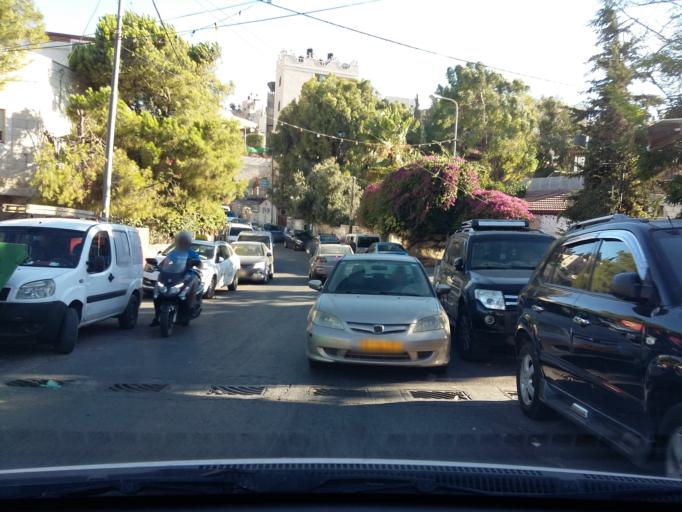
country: PS
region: West Bank
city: East Jerusalem
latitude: 31.7889
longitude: 35.2375
